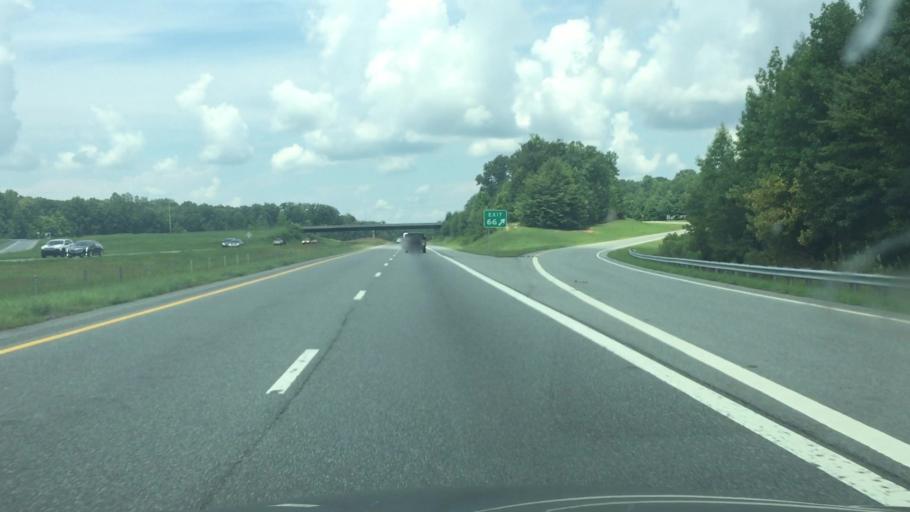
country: US
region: North Carolina
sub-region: Randolph County
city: Asheboro
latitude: 35.5896
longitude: -79.8112
